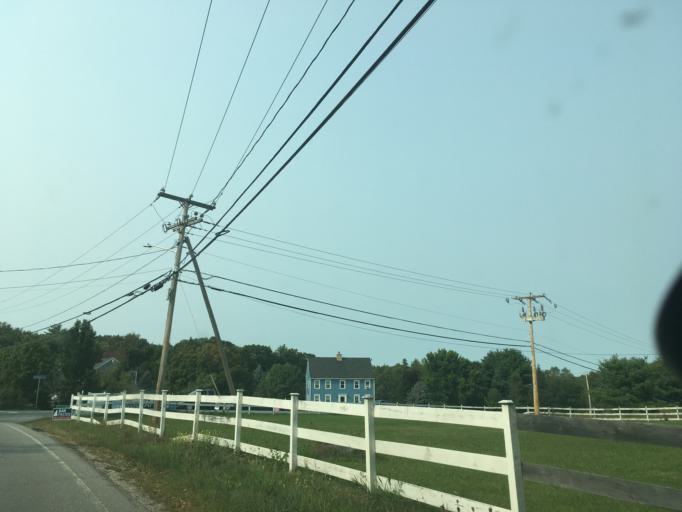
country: US
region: New Hampshire
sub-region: Rockingham County
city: Stratham Station
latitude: 42.9976
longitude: -70.8862
